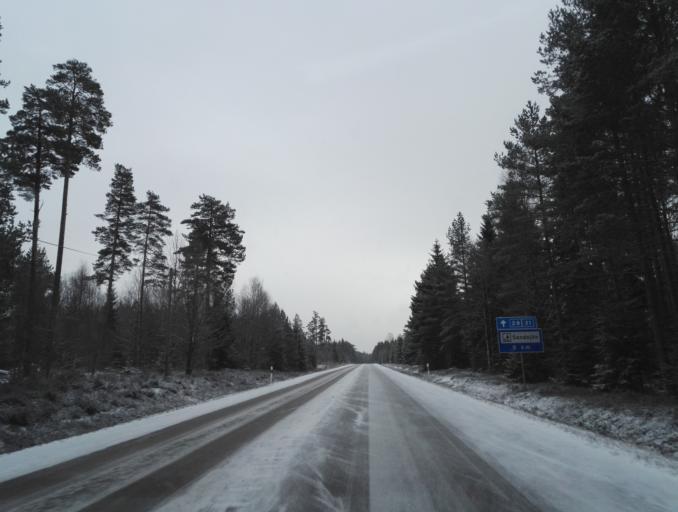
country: SE
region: Kronoberg
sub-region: Uppvidinge Kommun
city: Lenhovda
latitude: 56.9828
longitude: 15.2960
